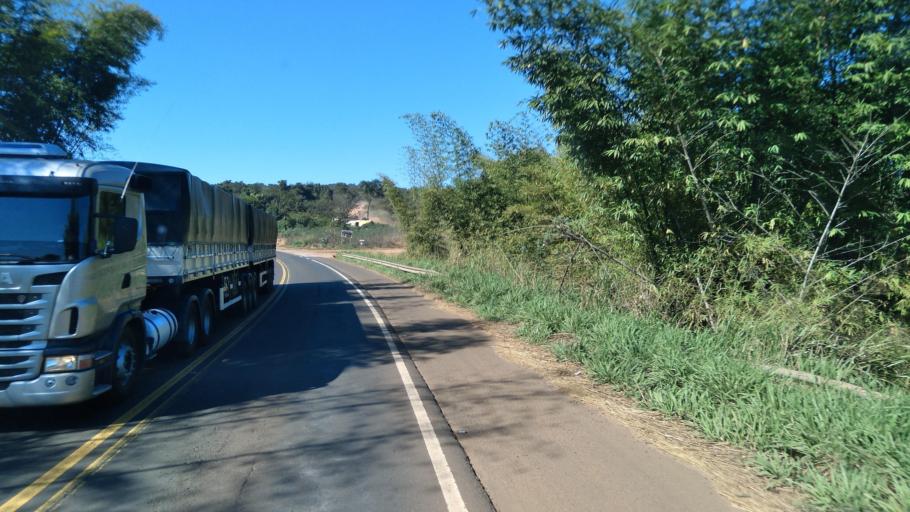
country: BR
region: Goias
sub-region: Mineiros
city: Mineiros
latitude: -17.5831
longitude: -52.5038
